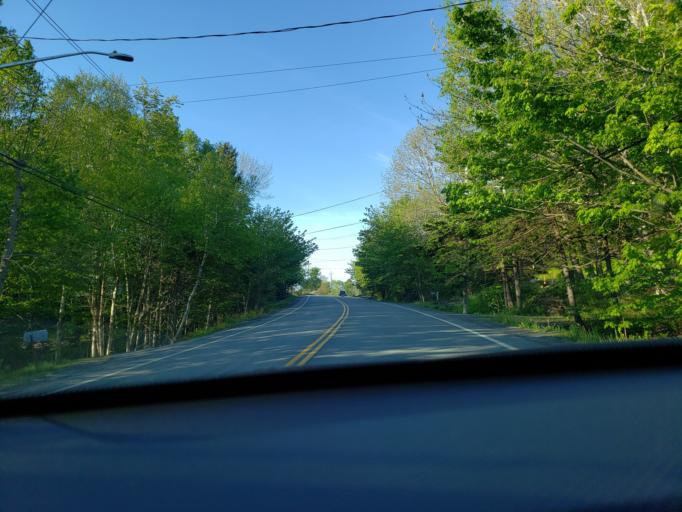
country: CA
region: Nova Scotia
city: Cole Harbour
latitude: 44.7324
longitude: -63.3931
